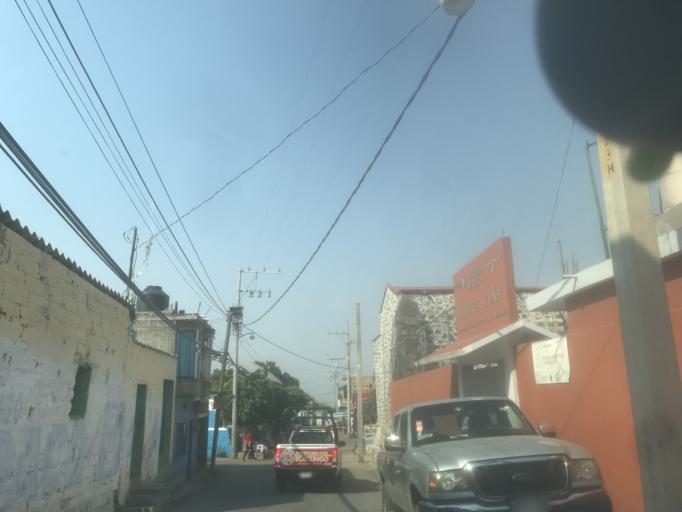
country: MX
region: Morelos
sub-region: Yecapixtla
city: Texcala
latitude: 18.9348
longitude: -98.7960
